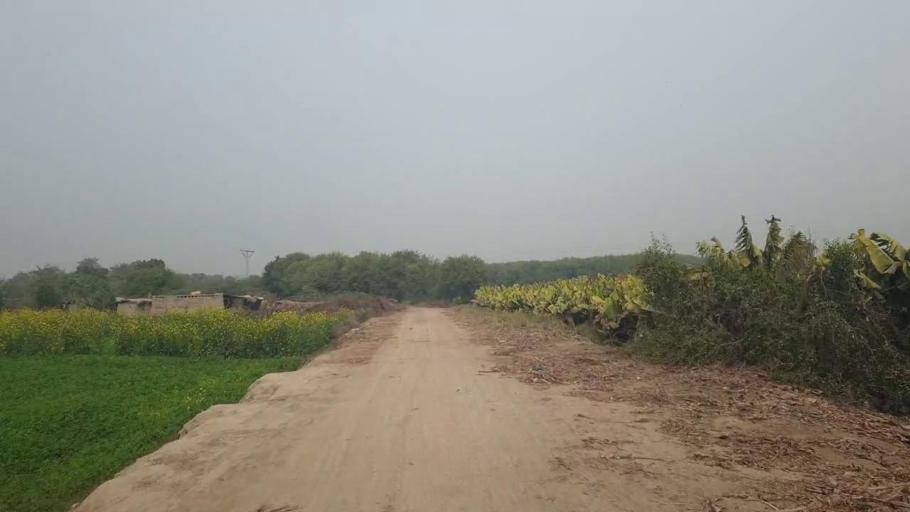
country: PK
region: Sindh
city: Tando Adam
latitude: 25.7160
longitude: 68.6156
